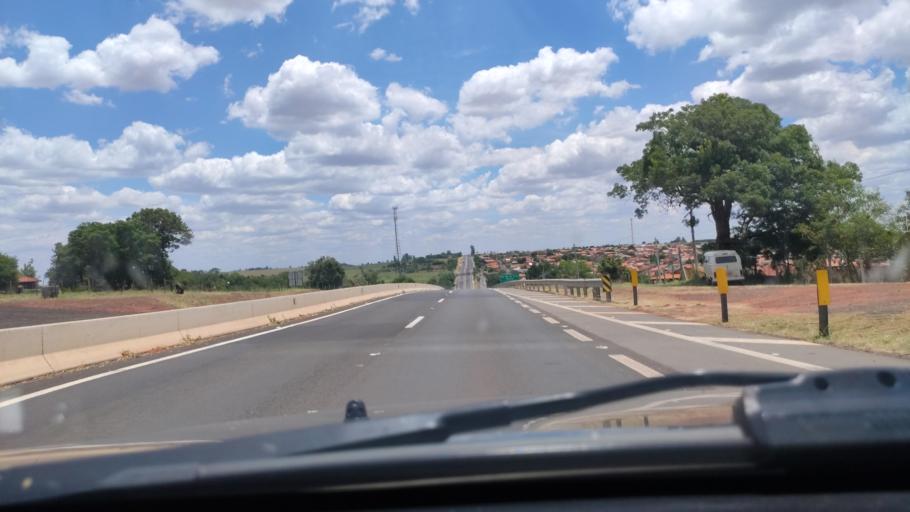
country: BR
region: Sao Paulo
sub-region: Duartina
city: Duartina
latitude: -22.6916
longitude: -49.4234
